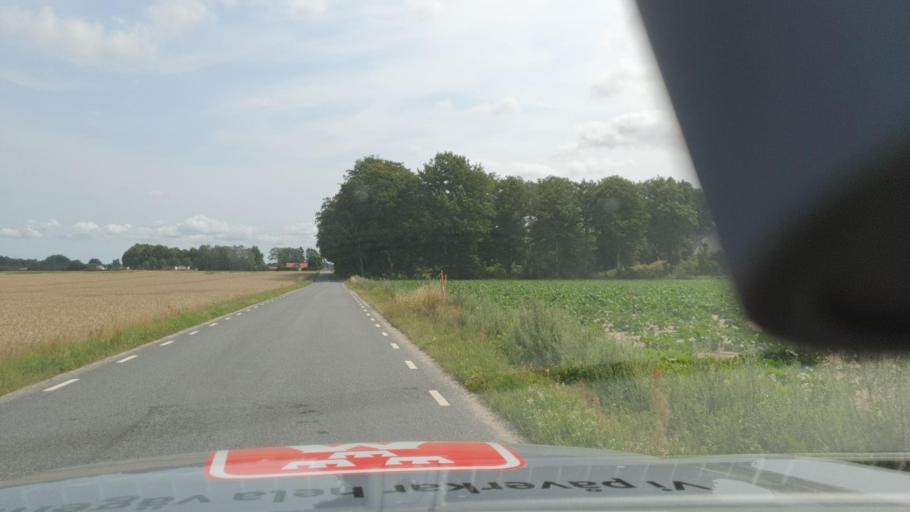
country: SE
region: Skane
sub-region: Bromolla Kommun
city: Bromoella
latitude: 56.0468
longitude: 14.3992
